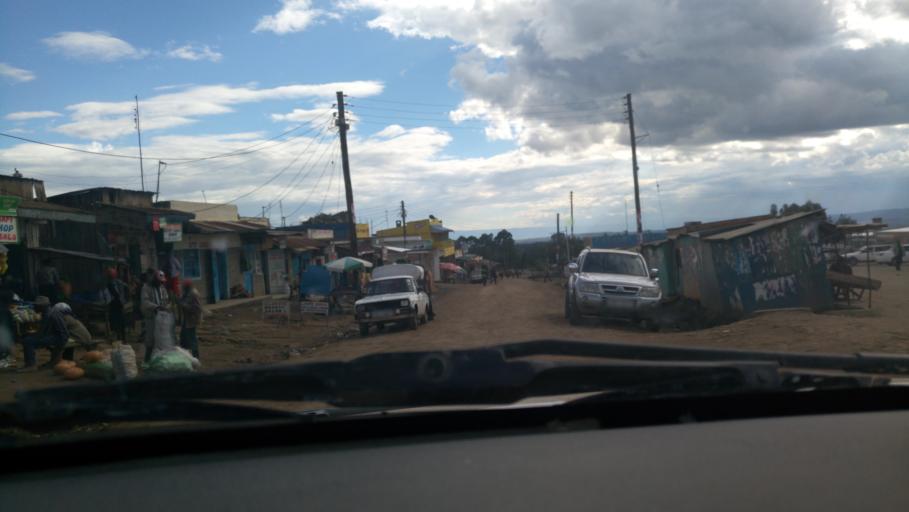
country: KE
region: Nyandarua
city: Ol Kalou
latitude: -0.3981
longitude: 36.4929
